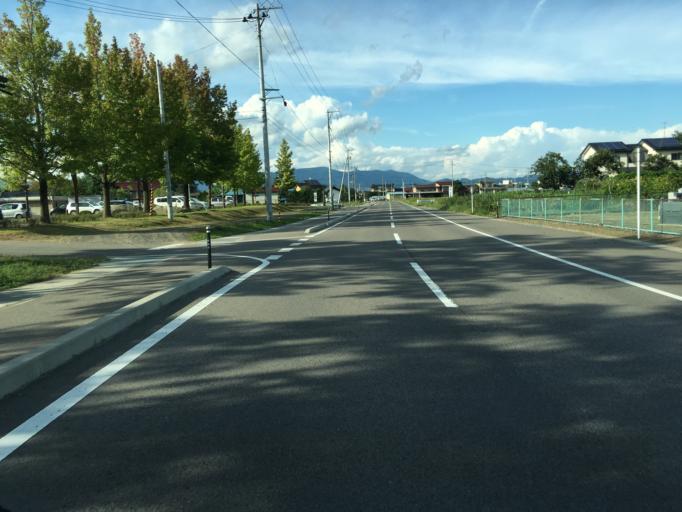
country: JP
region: Fukushima
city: Hobaramachi
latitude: 37.8188
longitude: 140.5716
